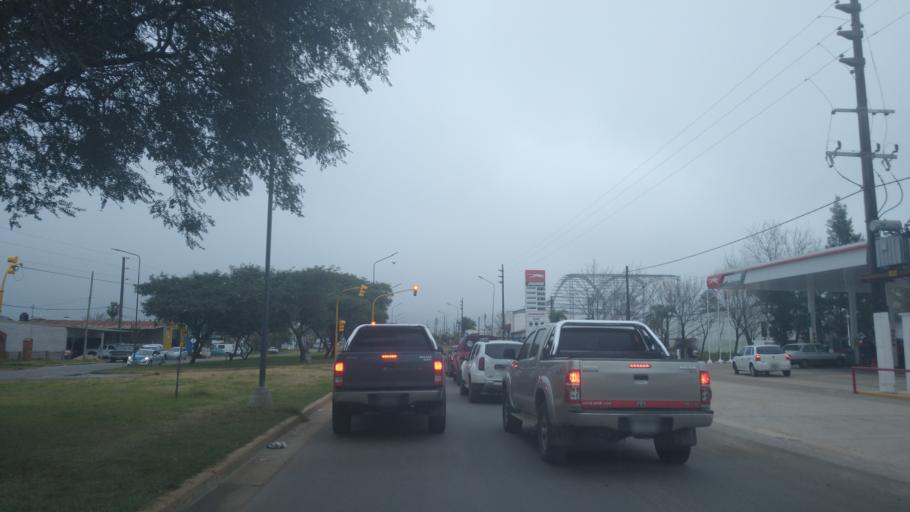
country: AR
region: Entre Rios
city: Chajari
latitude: -30.7612
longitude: -58.0058
